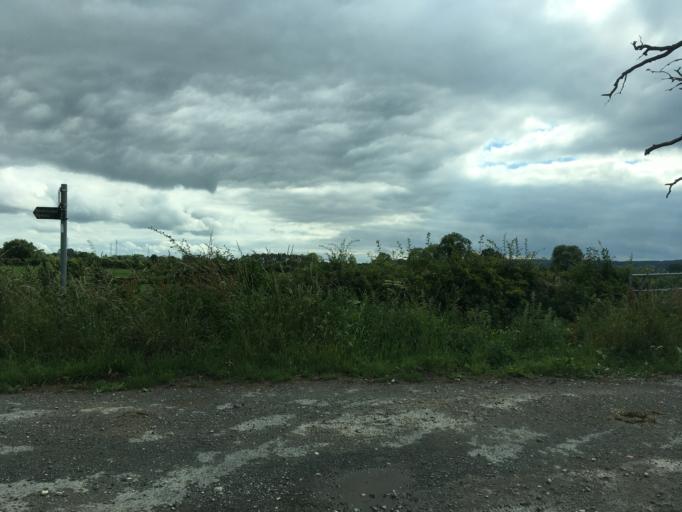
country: GB
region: England
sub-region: Gloucestershire
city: Cinderford
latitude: 51.8056
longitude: -2.4224
